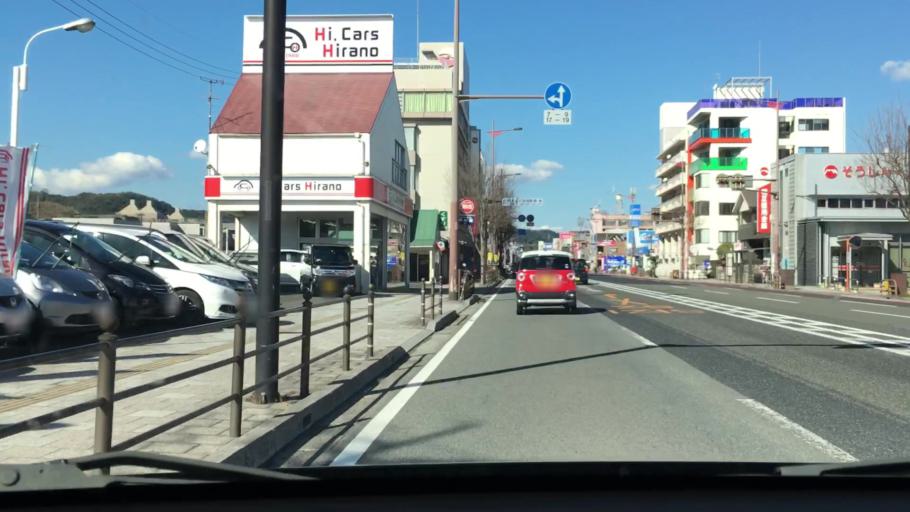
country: JP
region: Kagoshima
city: Kagoshima-shi
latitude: 31.6080
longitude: 130.5357
